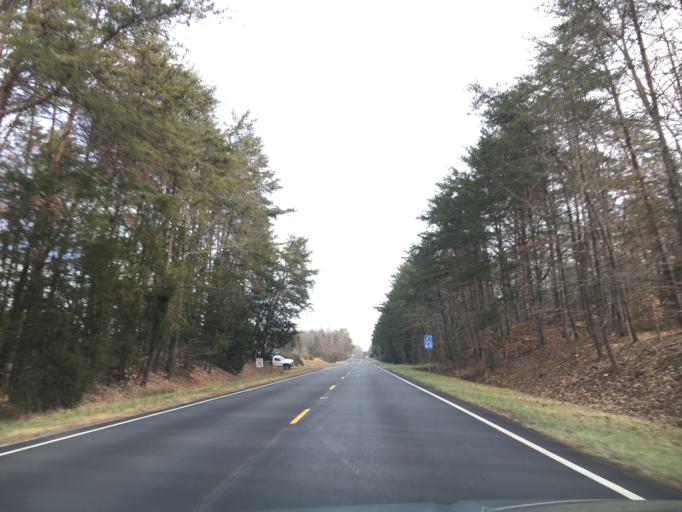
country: US
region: Virginia
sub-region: Goochland County
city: Goochland
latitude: 37.7781
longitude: -77.8933
